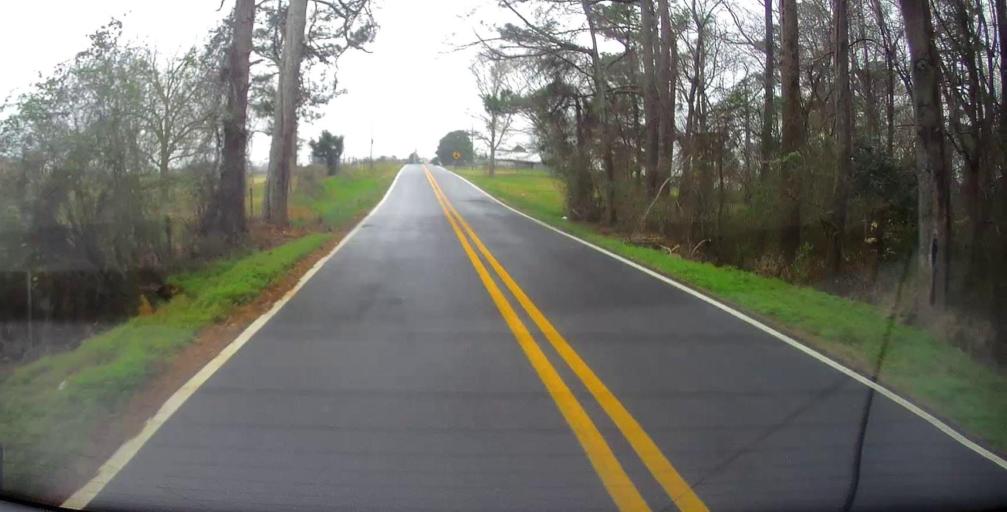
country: US
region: Georgia
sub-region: Monroe County
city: Forsyth
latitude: 33.0569
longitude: -83.8916
